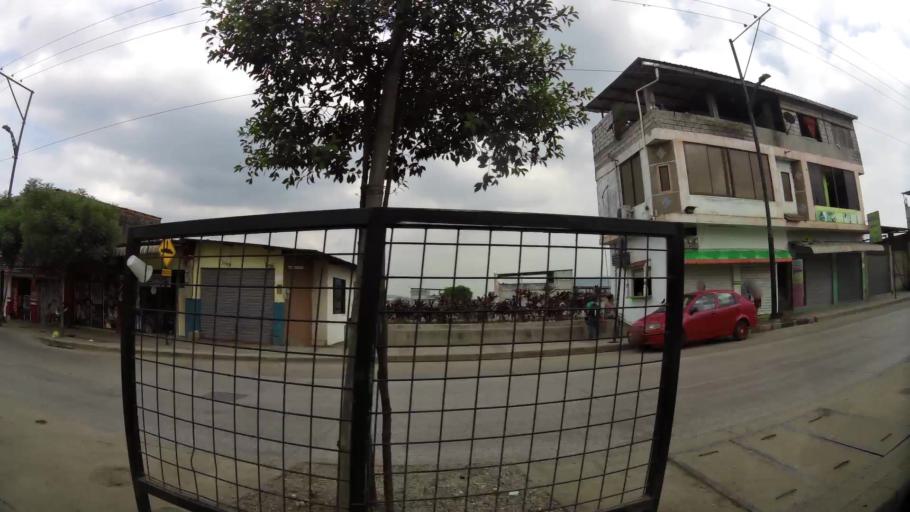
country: EC
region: Guayas
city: Santa Lucia
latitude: -2.1046
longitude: -79.9534
